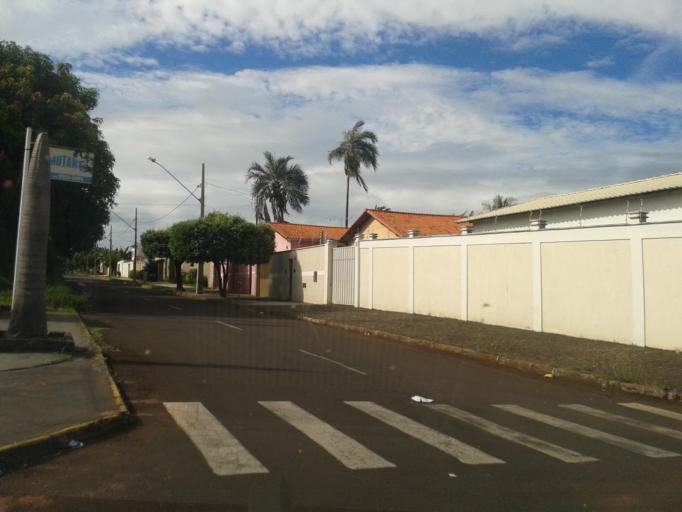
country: BR
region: Minas Gerais
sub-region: Ituiutaba
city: Ituiutaba
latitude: -18.9842
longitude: -49.4688
